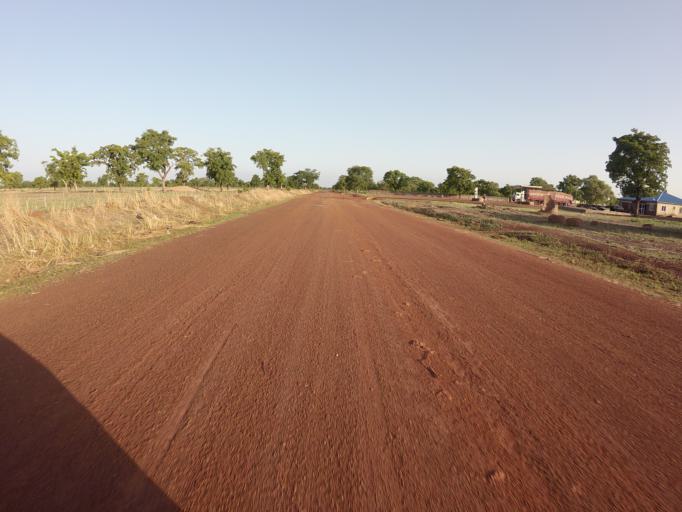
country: TG
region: Savanes
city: Sansanne-Mango
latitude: 10.3007
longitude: -0.0901
